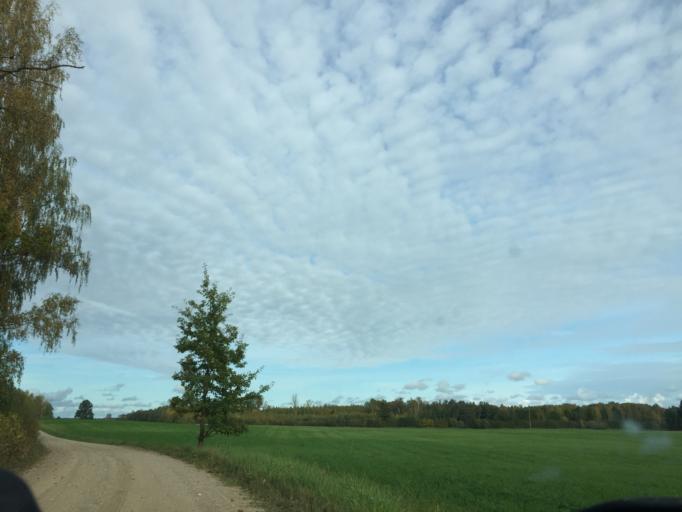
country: LV
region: Jaunpils
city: Jaunpils
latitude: 56.6386
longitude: 23.0755
